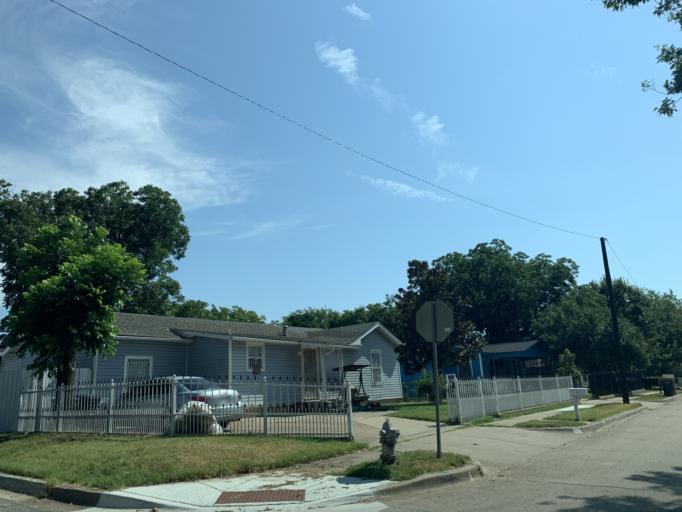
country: US
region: Texas
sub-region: Tarrant County
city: Fort Worth
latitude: 32.6962
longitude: -97.3185
